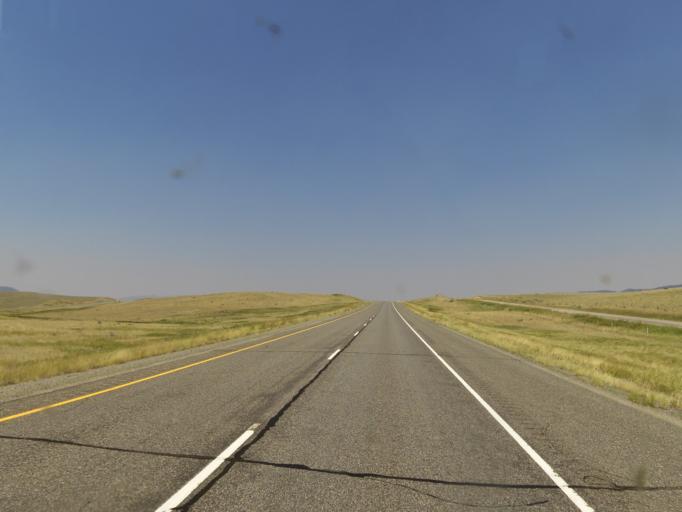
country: US
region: Montana
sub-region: Silver Bow County
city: Butte-Silver Bow (Balance)
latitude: 45.8968
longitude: -112.6706
